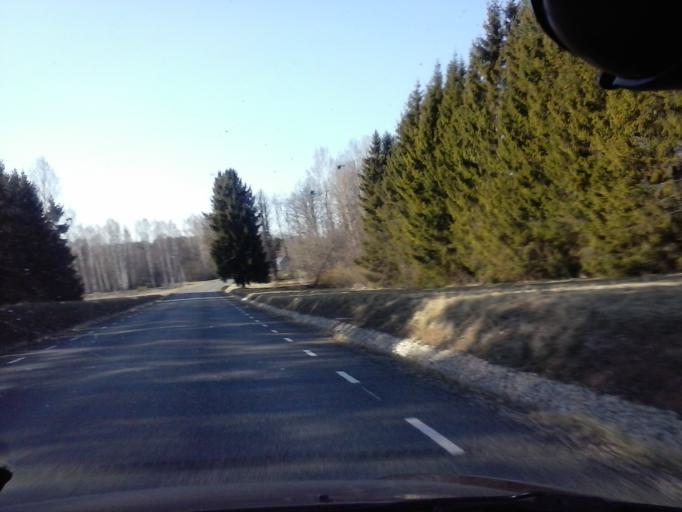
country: EE
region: Tartu
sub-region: UElenurme vald
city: Ulenurme
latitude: 58.1720
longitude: 26.8344
